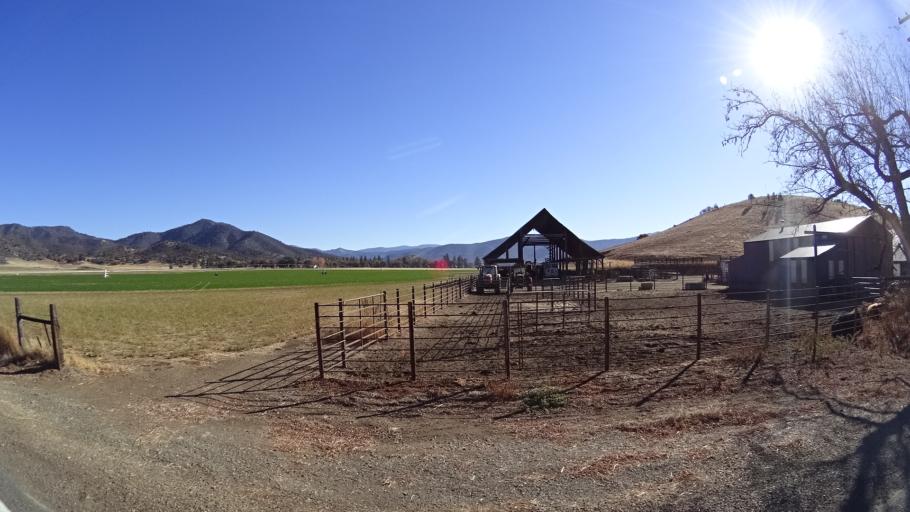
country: US
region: California
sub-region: Siskiyou County
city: Yreka
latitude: 41.5712
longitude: -122.8362
